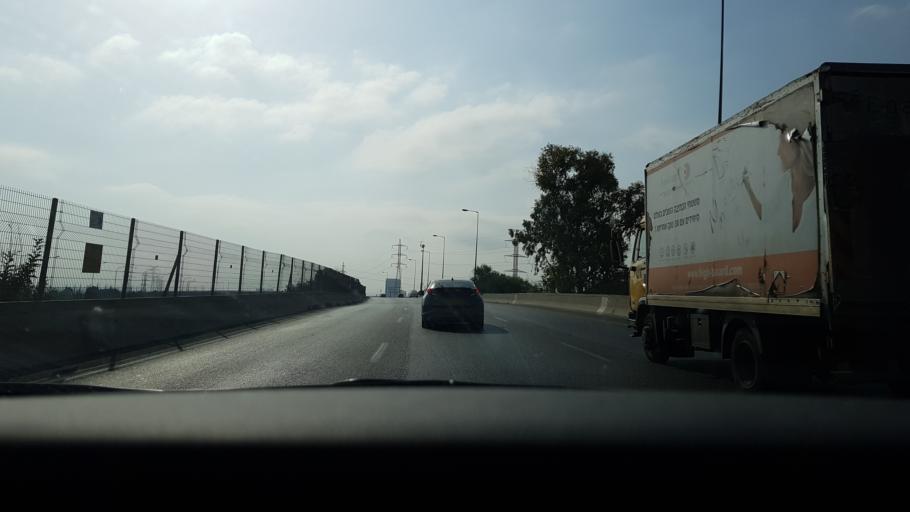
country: IL
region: Tel Aviv
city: Azor
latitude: 32.0422
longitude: 34.7887
